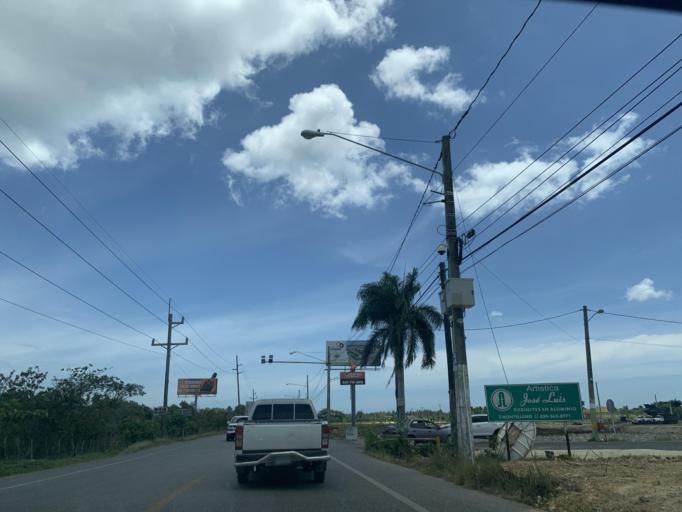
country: DO
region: Puerto Plata
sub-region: Puerto Plata
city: Puerto Plata
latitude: 19.7395
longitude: -70.6022
